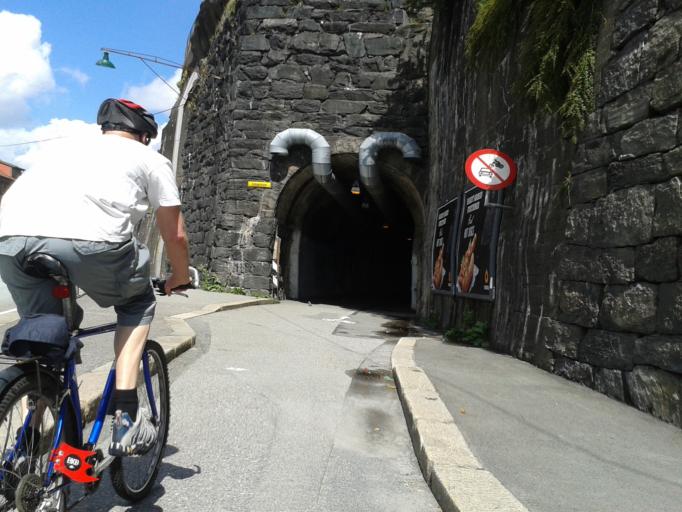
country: NO
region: Hordaland
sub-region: Bergen
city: Bergen
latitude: 60.4033
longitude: 5.3215
